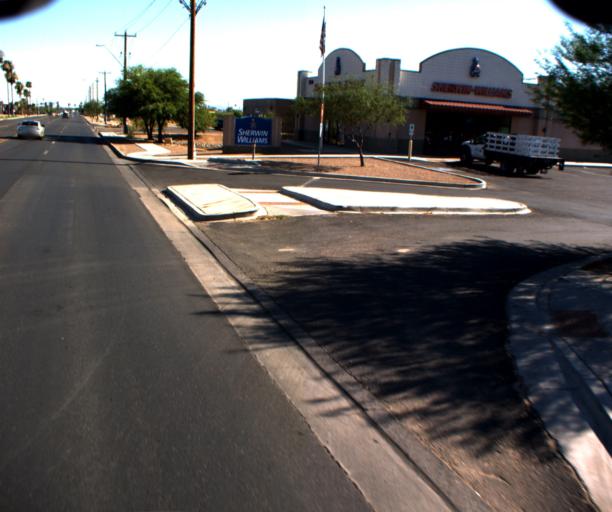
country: US
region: Arizona
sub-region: Pinal County
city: Casa Grande
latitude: 32.8909
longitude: -111.7572
